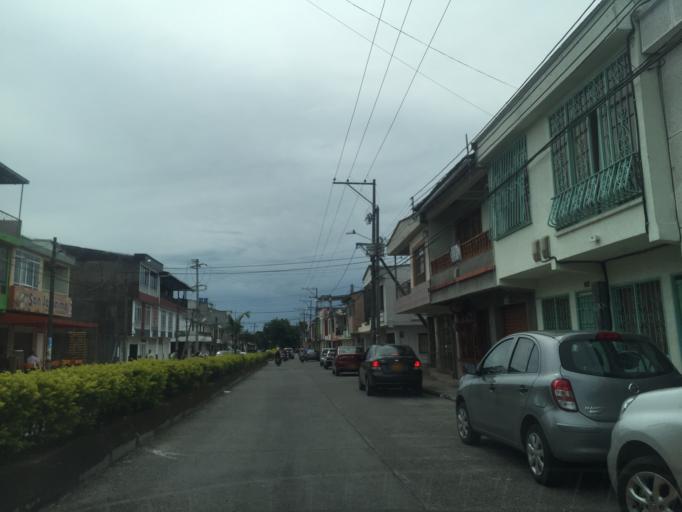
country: CO
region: Quindio
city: Montenegro
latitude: 4.5619
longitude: -75.7481
